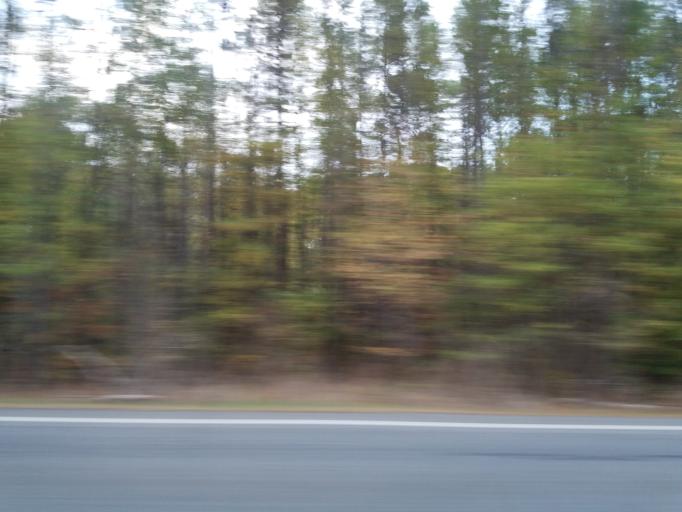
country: US
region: Georgia
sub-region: Murray County
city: Chatsworth
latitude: 34.5918
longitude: -84.6914
